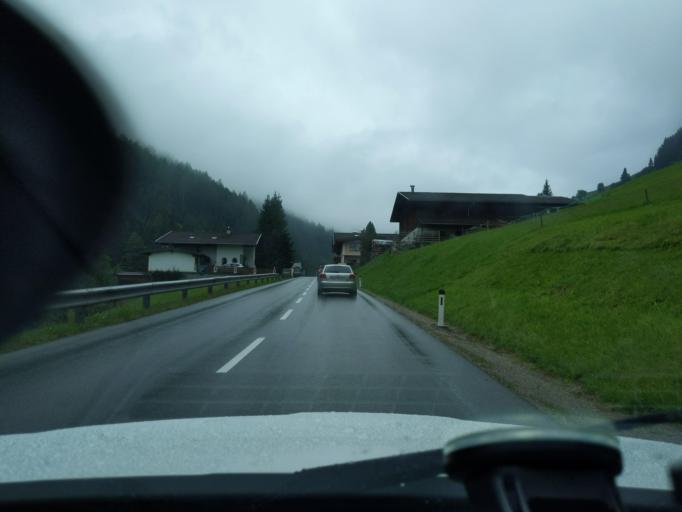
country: AT
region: Tyrol
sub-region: Politischer Bezirk Schwaz
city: Mayrhofen
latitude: 47.1503
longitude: 11.7927
